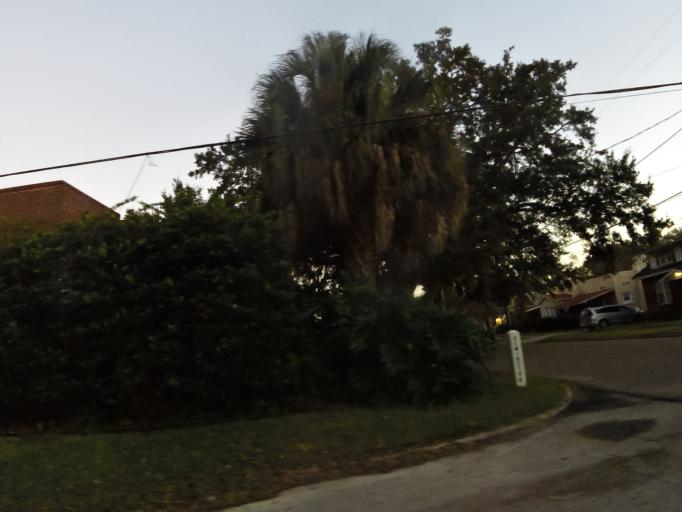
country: US
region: Florida
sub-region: Duval County
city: Jacksonville
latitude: 30.3038
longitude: -81.7120
